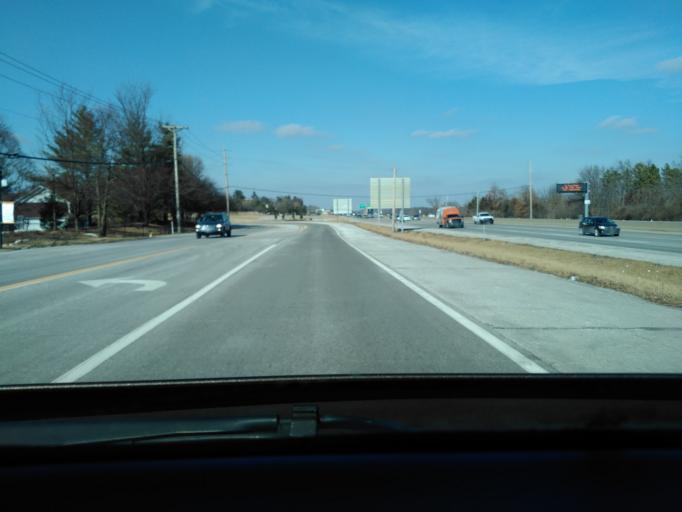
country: US
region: Missouri
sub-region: Saint Louis County
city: Manchester
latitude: 38.6318
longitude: -90.5143
